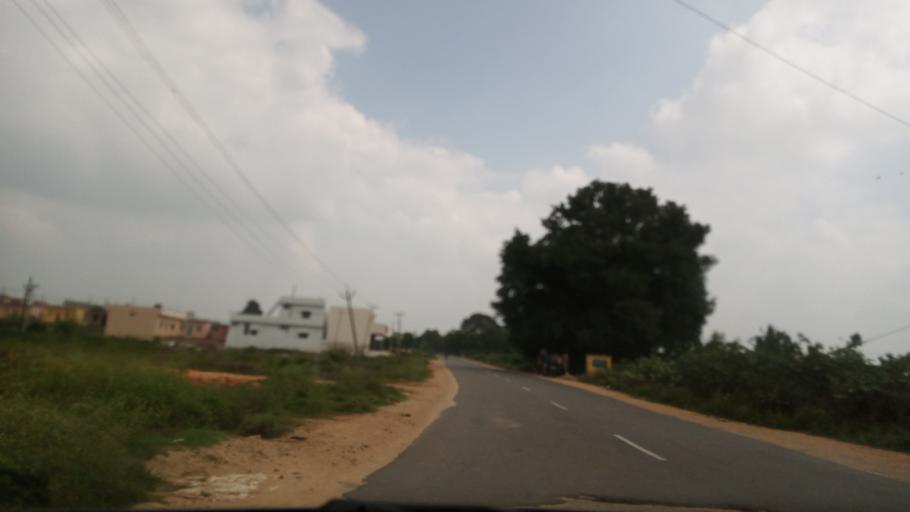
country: IN
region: Andhra Pradesh
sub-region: Chittoor
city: Madanapalle
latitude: 13.6372
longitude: 78.6372
